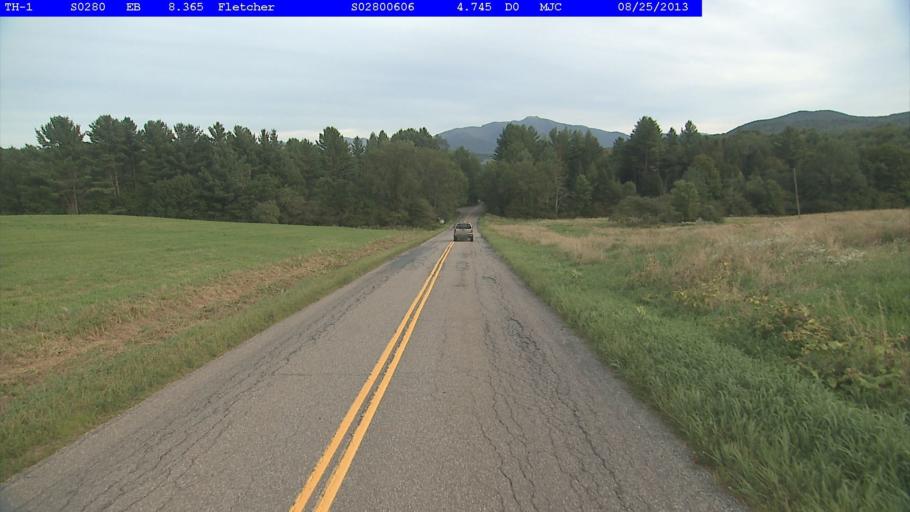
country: US
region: Vermont
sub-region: Chittenden County
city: Jericho
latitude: 44.6640
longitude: -72.8889
